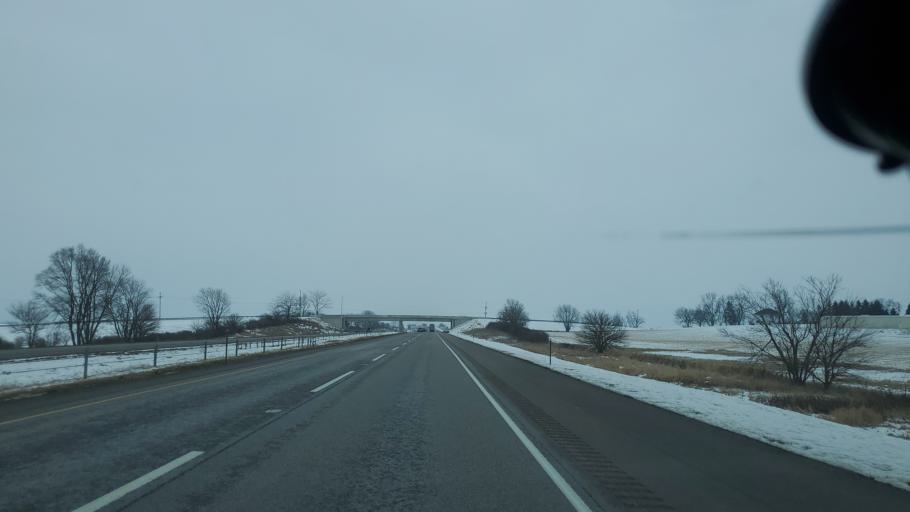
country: US
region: Illinois
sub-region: Kane County
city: Maple Park
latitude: 41.8970
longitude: -88.6428
